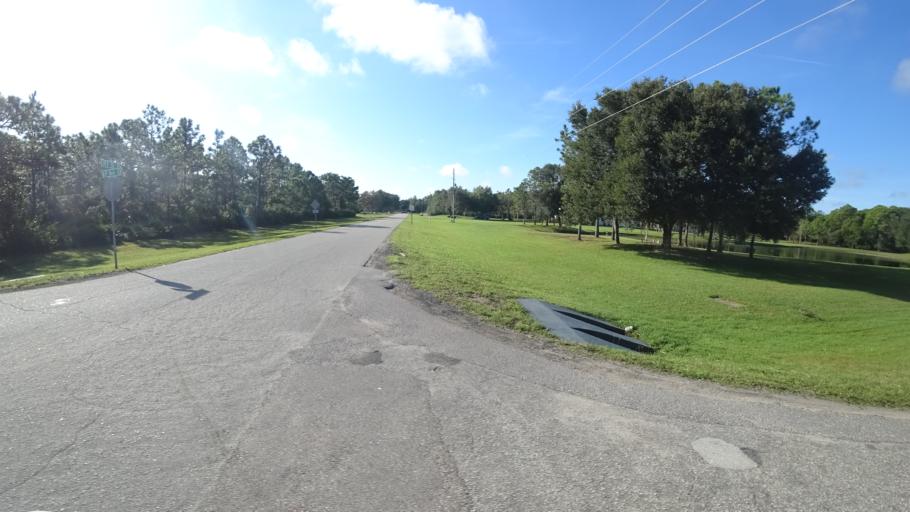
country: US
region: Florida
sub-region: Sarasota County
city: The Meadows
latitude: 27.4169
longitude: -82.3404
